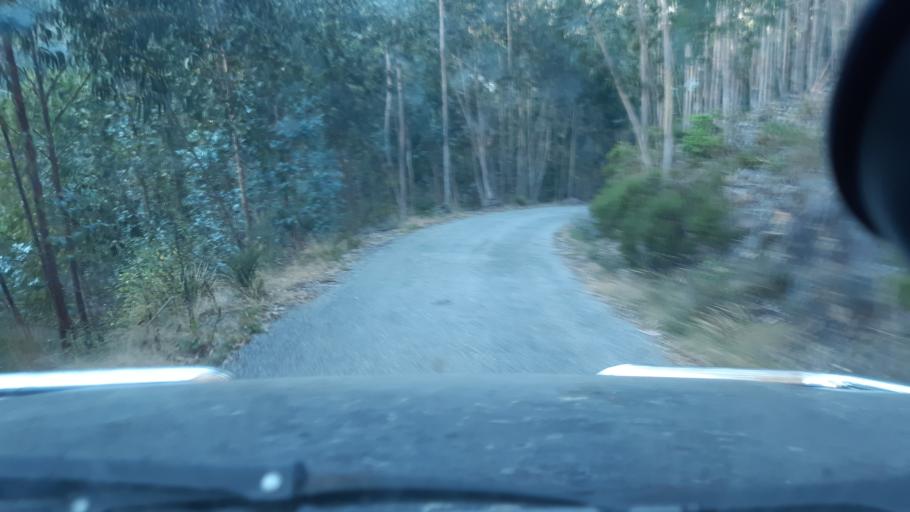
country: PT
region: Viseu
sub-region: Mortagua
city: Mortagua
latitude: 40.5276
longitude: -8.2561
